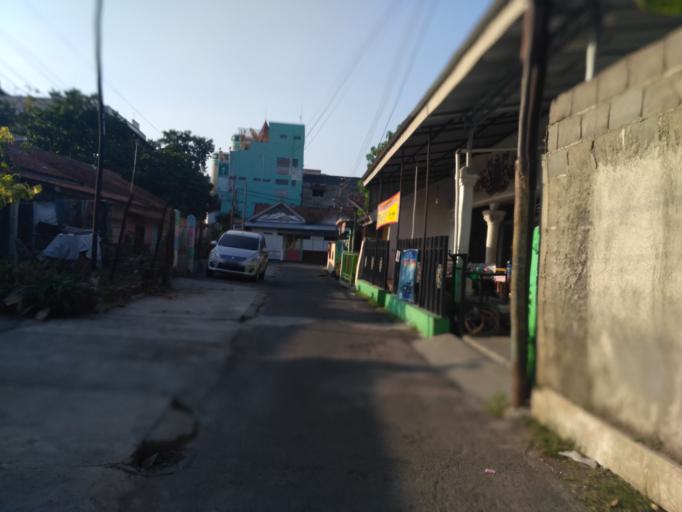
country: ID
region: Central Java
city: Semarang
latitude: -7.0059
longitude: 110.4296
